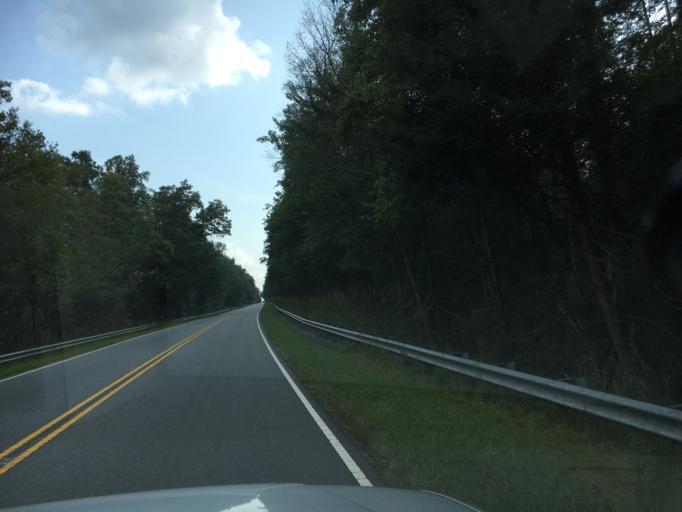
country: US
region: North Carolina
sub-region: Rutherford County
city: Rutherfordton
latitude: 35.4560
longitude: -81.9790
